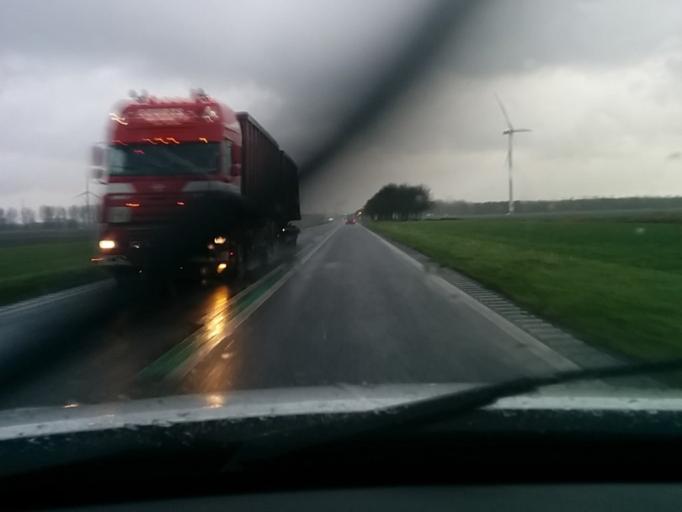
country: NL
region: Utrecht
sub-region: Gemeente Bunschoten
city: Bunschoten
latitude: 52.3207
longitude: 5.4209
